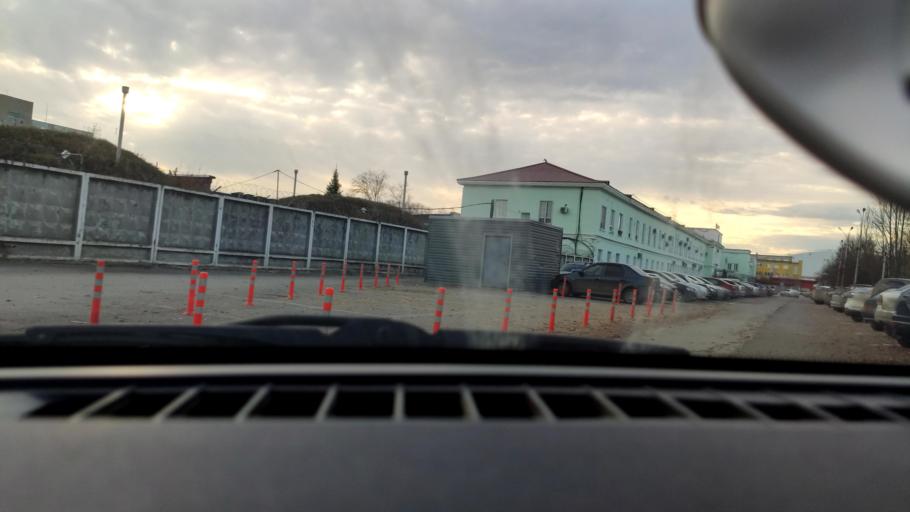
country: RU
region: Perm
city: Perm
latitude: 57.9657
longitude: 56.2471
